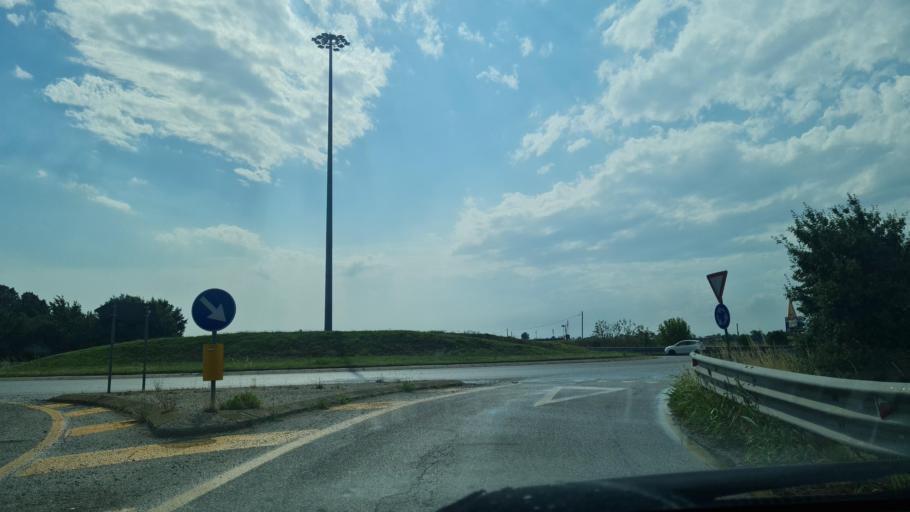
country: IT
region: Piedmont
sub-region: Provincia di Novara
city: Cameri
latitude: 45.5051
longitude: 8.6335
